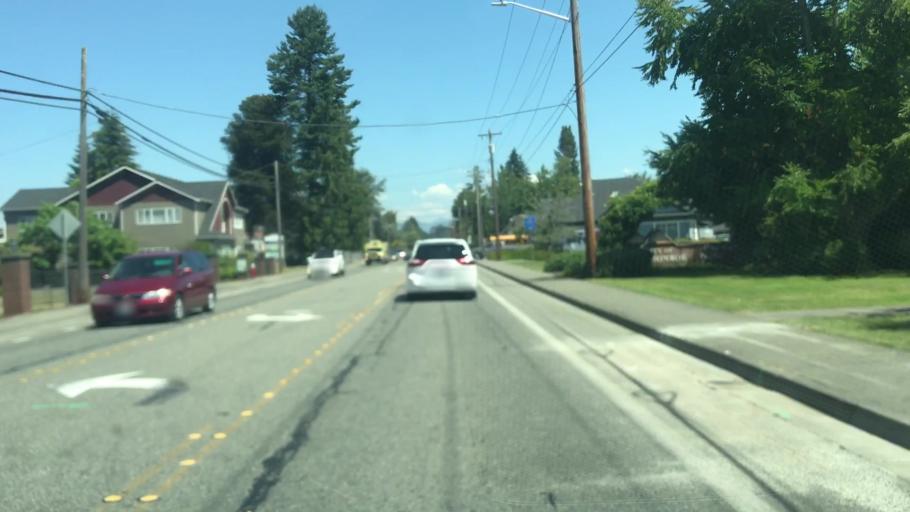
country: US
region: Washington
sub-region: Snohomish County
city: Monroe
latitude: 47.8521
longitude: -121.9823
